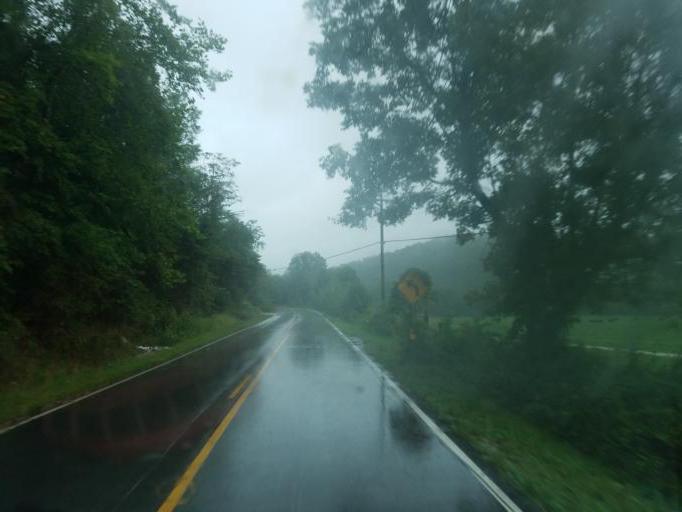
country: US
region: Kentucky
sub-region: Carter County
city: Grayson
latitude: 38.4730
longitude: -83.0364
